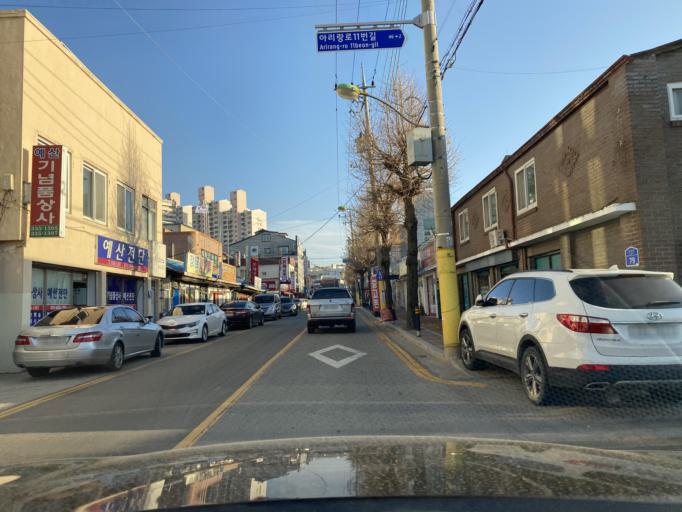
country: KR
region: Chungcheongnam-do
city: Yesan
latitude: 36.6882
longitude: 126.8305
